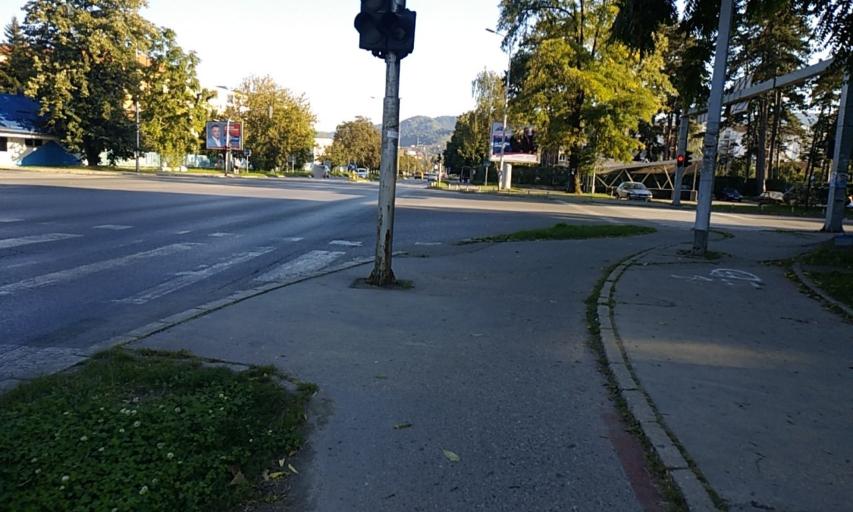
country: BA
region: Republika Srpska
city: Starcevica
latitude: 44.7750
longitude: 17.2074
